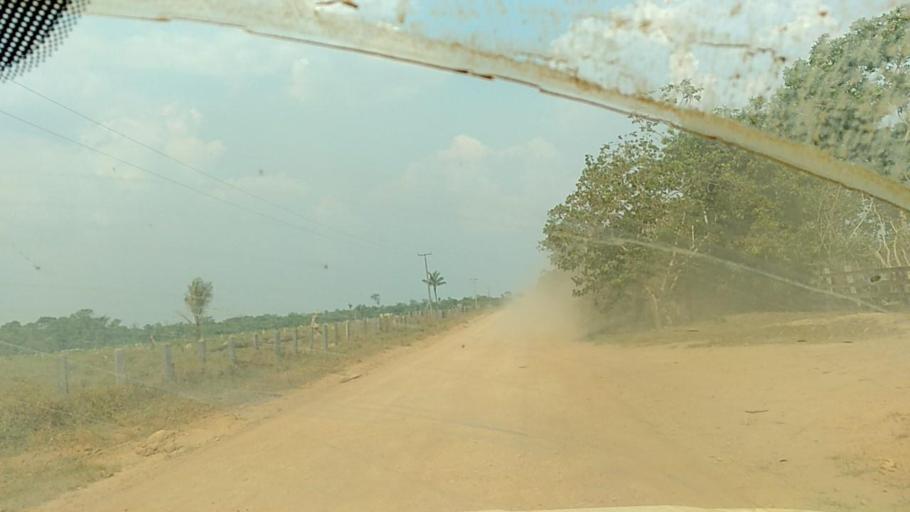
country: BR
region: Rondonia
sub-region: Porto Velho
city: Porto Velho
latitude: -8.6832
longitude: -63.2157
